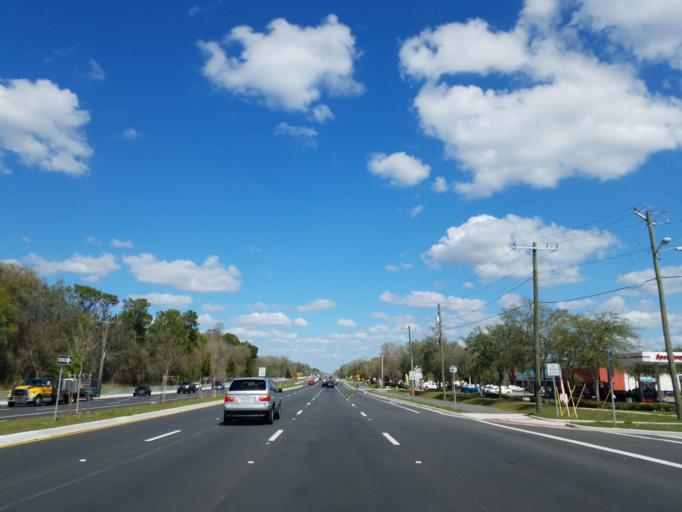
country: US
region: Florida
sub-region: Hillsborough County
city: University
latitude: 28.0822
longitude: -82.4135
